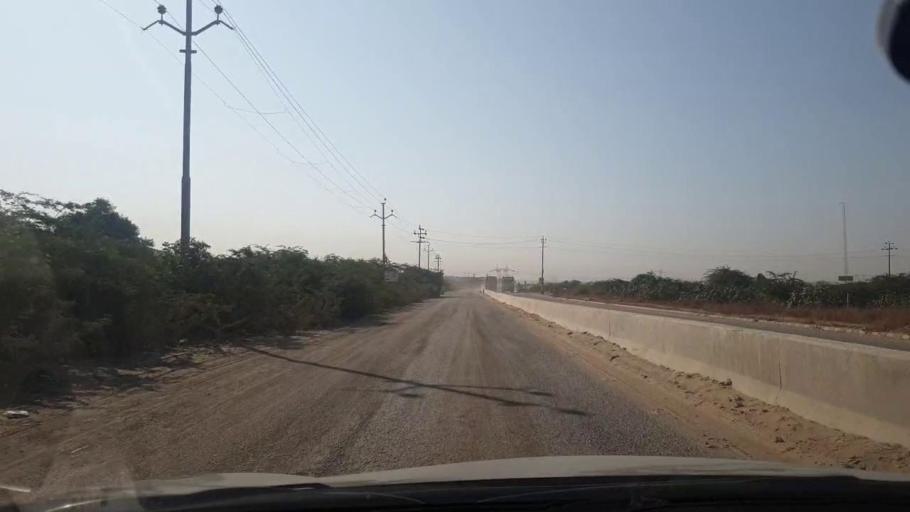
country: PK
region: Sindh
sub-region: Karachi District
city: Karachi
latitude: 25.0777
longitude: 67.0138
